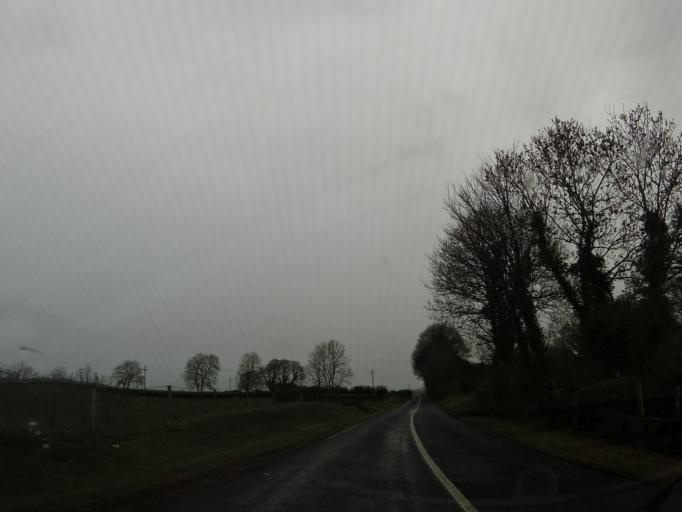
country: IE
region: Connaught
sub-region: Sligo
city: Collooney
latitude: 54.1741
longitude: -8.5084
